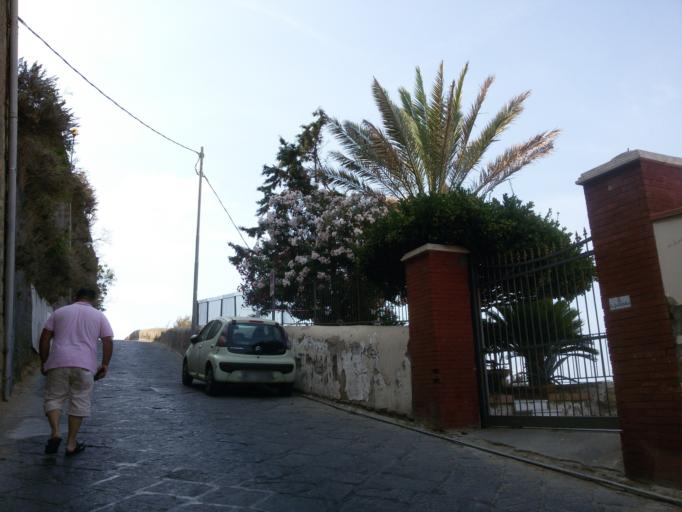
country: IT
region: Campania
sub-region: Provincia di Napoli
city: Procida
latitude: 40.7616
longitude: 14.0323
